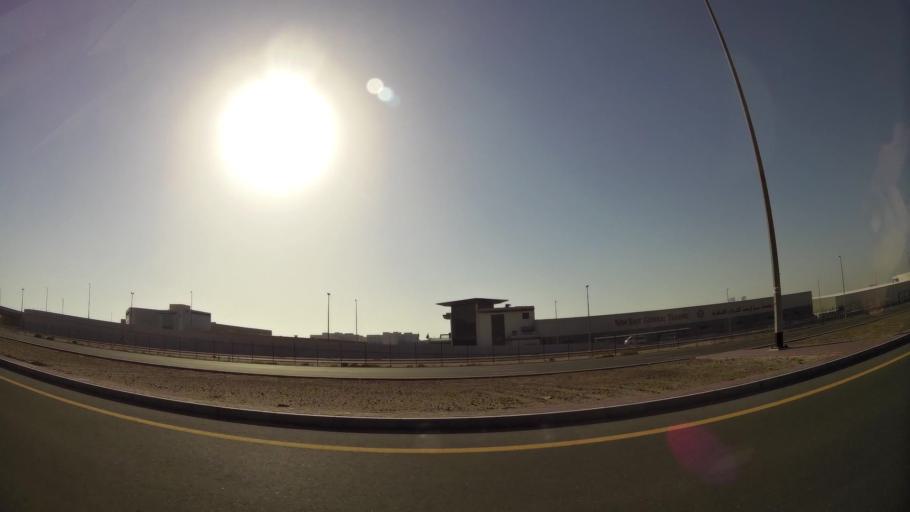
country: AE
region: Dubai
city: Dubai
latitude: 24.9443
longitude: 55.0876
